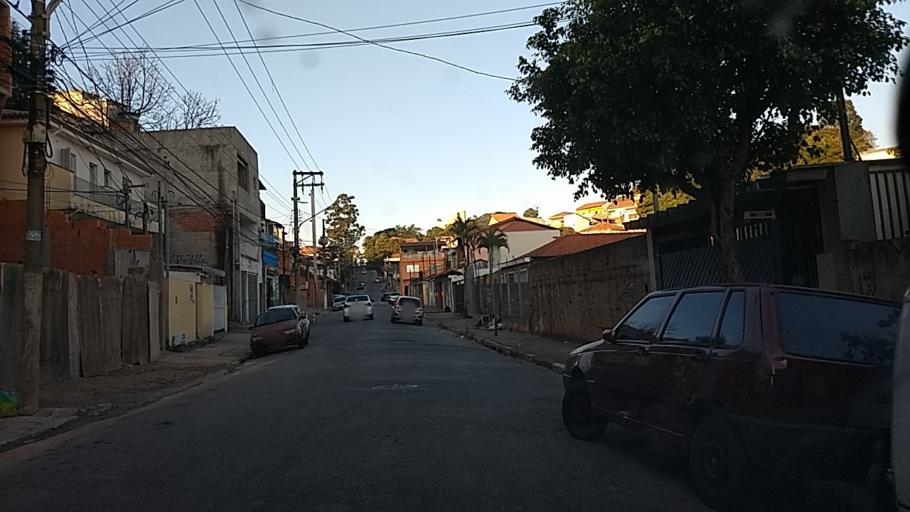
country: BR
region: Sao Paulo
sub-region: Sao Paulo
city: Sao Paulo
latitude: -23.4930
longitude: -46.6052
